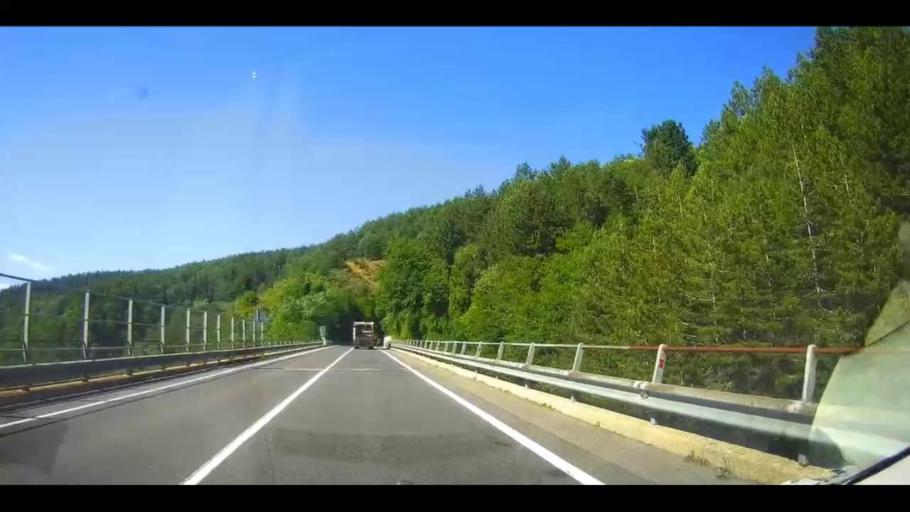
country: IT
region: Calabria
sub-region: Provincia di Cosenza
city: Celico
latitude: 39.3336
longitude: 16.3602
